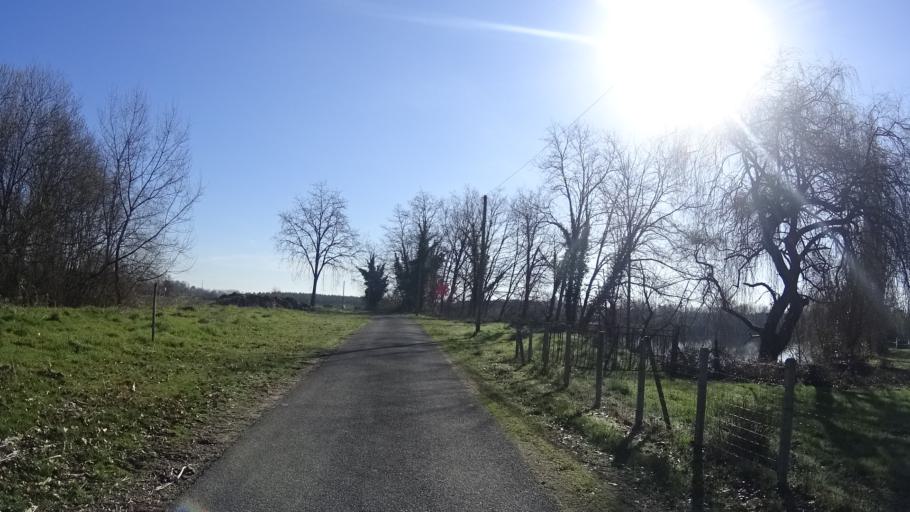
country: FR
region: Aquitaine
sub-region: Departement de la Dordogne
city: Montpon-Menesterol
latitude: 45.0338
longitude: 0.2272
